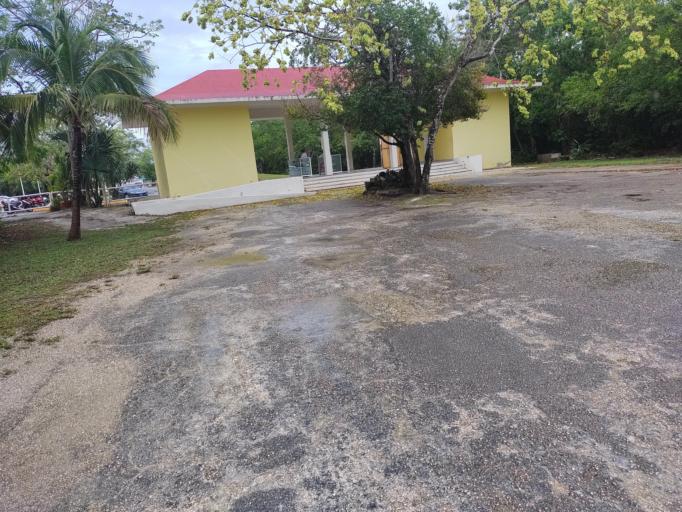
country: MX
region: Quintana Roo
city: San Miguel de Cozumel
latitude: 20.4895
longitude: -86.9406
